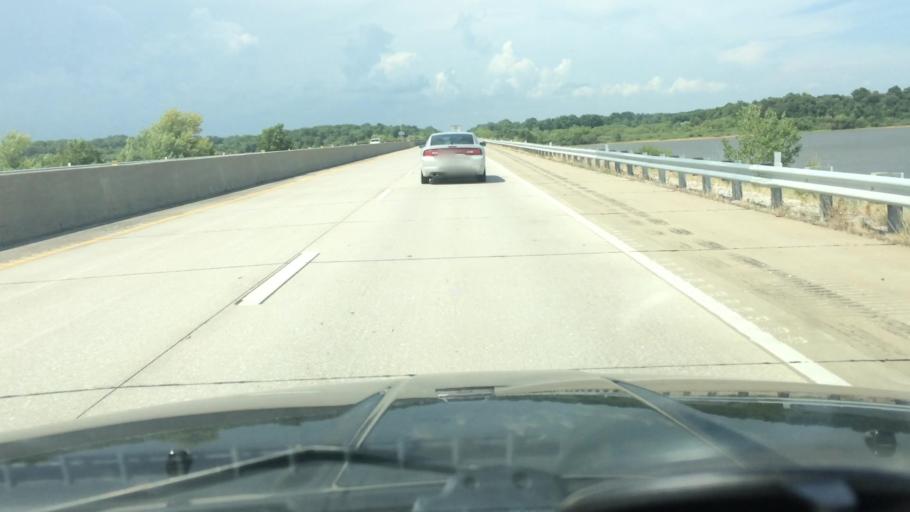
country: US
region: Missouri
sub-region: Henry County
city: Clinton
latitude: 38.2831
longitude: -93.7594
